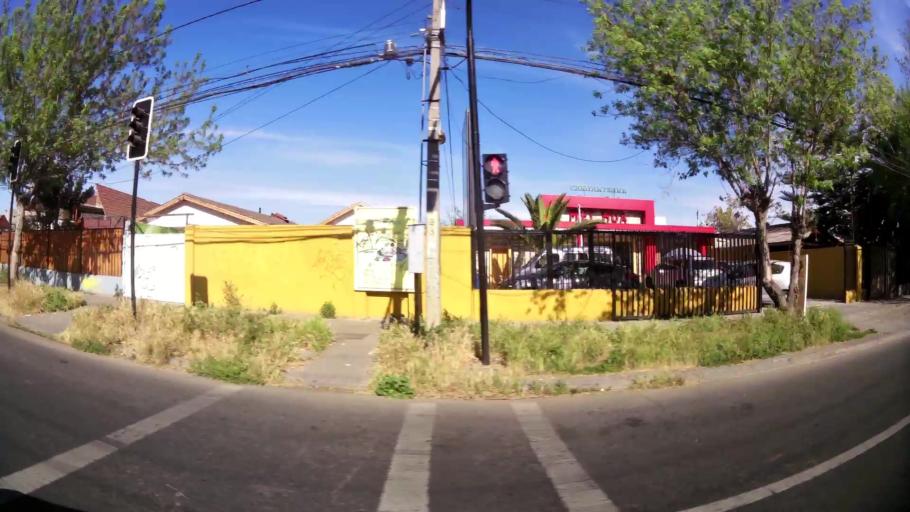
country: CL
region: Santiago Metropolitan
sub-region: Provincia de Santiago
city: Lo Prado
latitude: -33.4717
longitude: -70.7367
